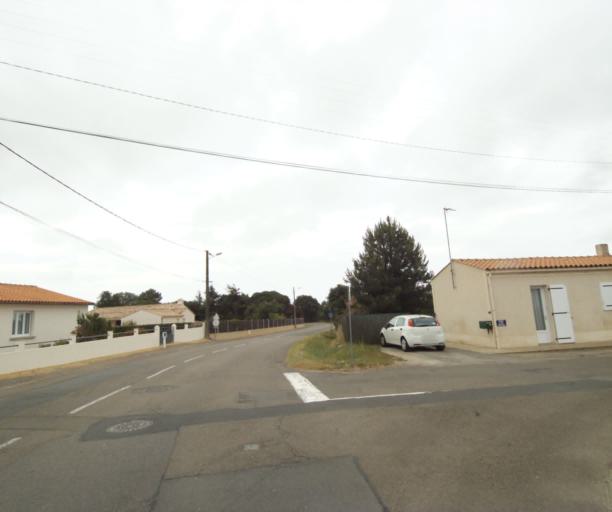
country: FR
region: Pays de la Loire
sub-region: Departement de la Vendee
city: Chateau-d'Olonne
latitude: 46.5012
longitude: -1.7331
